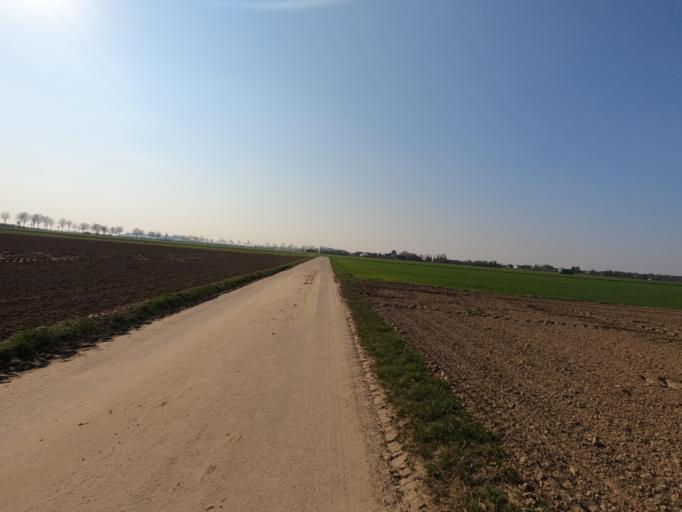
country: DE
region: North Rhine-Westphalia
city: Huckelhoven
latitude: 51.0947
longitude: 6.2505
